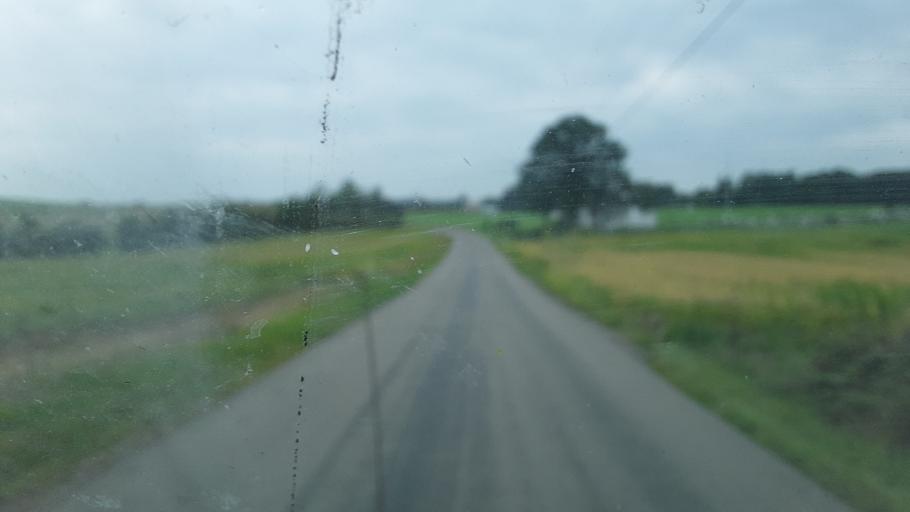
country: US
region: Pennsylvania
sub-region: Jefferson County
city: Punxsutawney
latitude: 40.9469
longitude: -79.1448
